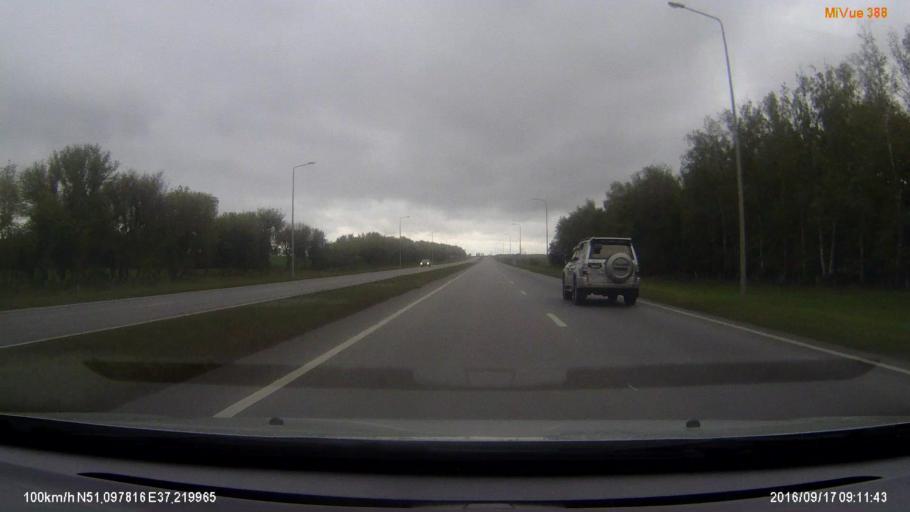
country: RU
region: Belgorod
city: Skorodnoye
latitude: 51.0973
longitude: 37.2197
